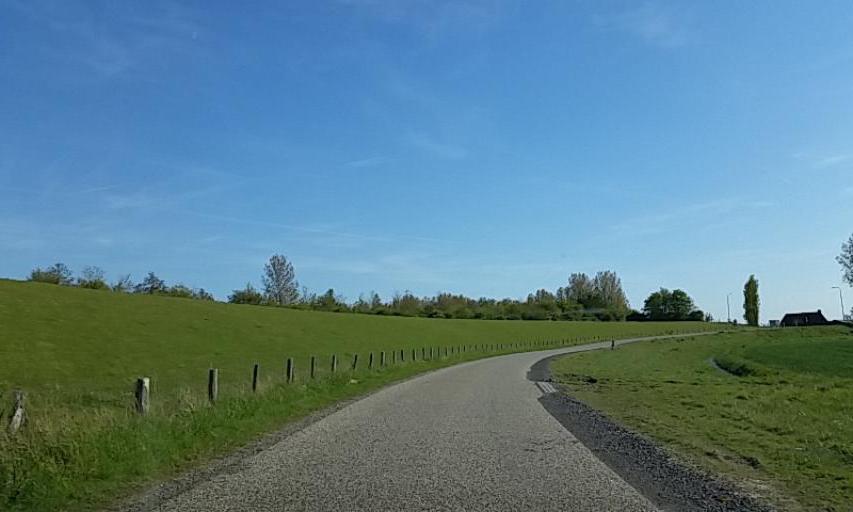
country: NL
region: Zeeland
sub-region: Gemeente Borsele
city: Borssele
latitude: 51.3444
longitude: 3.7336
